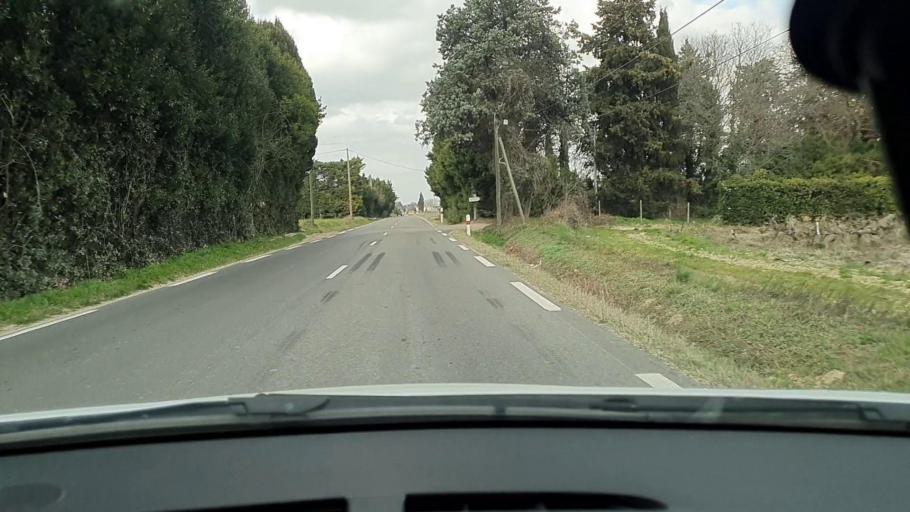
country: FR
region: Languedoc-Roussillon
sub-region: Departement du Gard
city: Meynes
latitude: 43.8934
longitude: 4.5735
